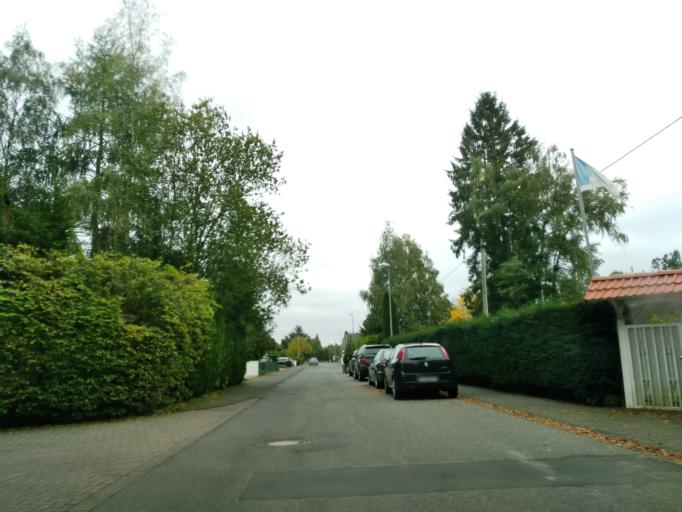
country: DE
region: Rheinland-Pfalz
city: Windhagen
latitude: 50.6395
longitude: 7.3205
